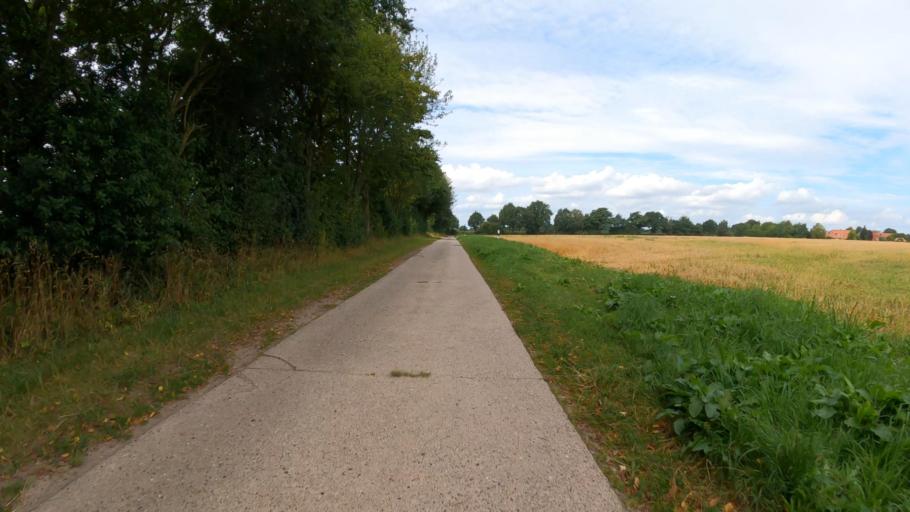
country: DE
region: Lower Saxony
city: Neu Wulmstorf
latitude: 53.4323
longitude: 9.8077
